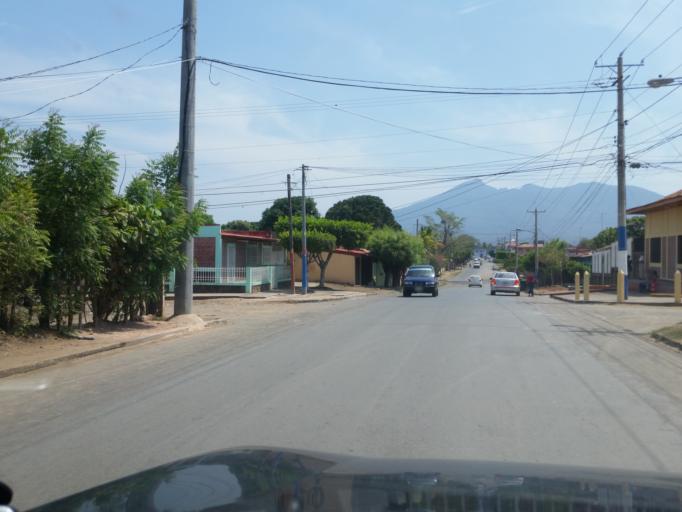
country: NI
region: Granada
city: Granada
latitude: 11.9395
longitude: -85.9621
